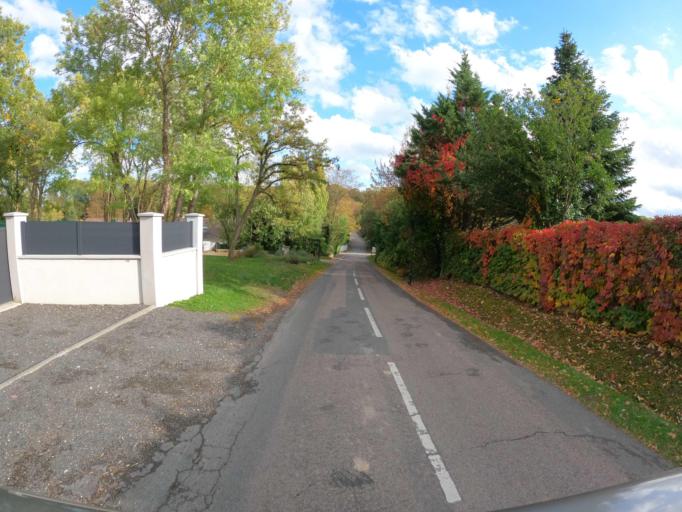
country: FR
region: Ile-de-France
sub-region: Departement de Seine-et-Marne
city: Coupvray
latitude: 48.8910
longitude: 2.7891
